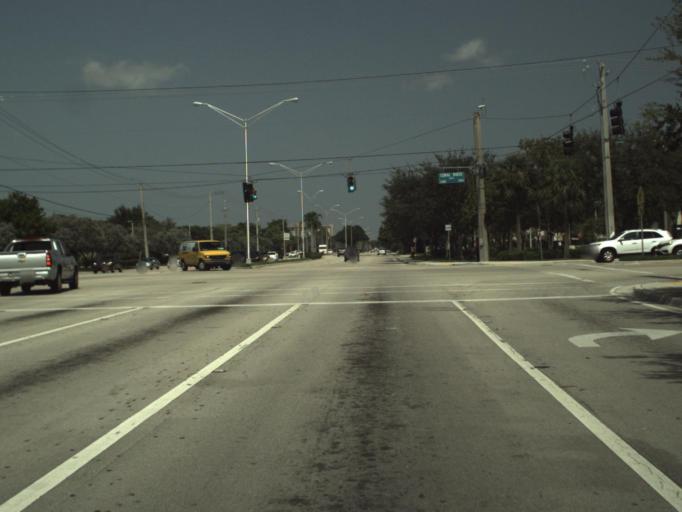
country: US
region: Florida
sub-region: Broward County
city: Coral Springs
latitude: 26.2727
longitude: -80.2829
